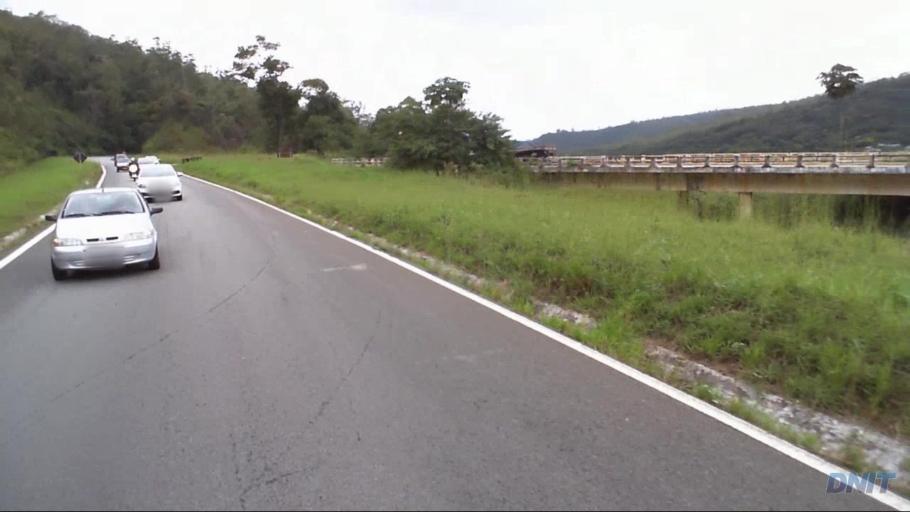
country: BR
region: Minas Gerais
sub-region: Joao Monlevade
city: Joao Monlevade
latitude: -19.8606
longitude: -43.1162
